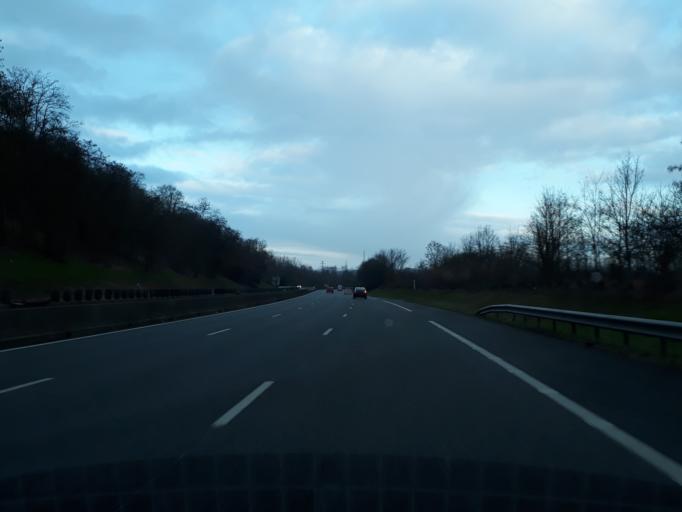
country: FR
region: Picardie
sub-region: Departement de l'Oise
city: Pontpoint
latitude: 49.3012
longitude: 2.6885
